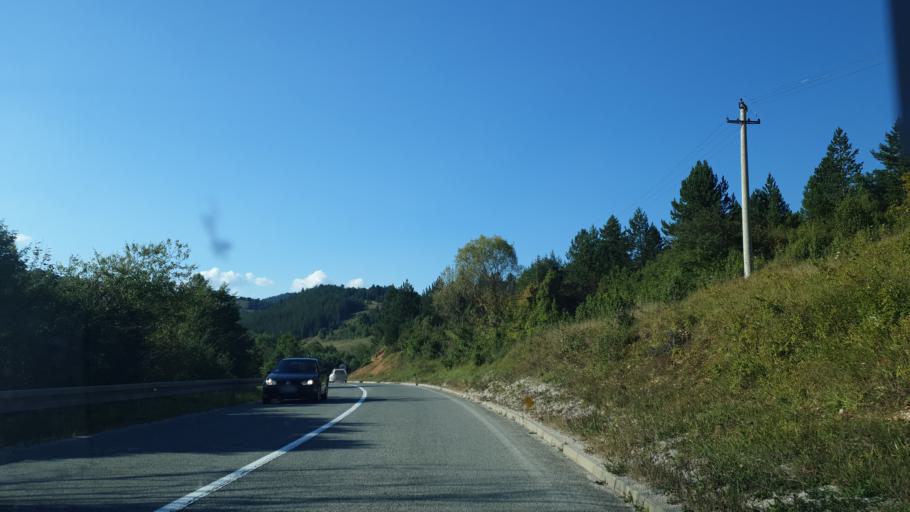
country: RS
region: Central Serbia
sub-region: Zlatiborski Okrug
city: Nova Varos
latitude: 43.5469
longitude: 19.7827
